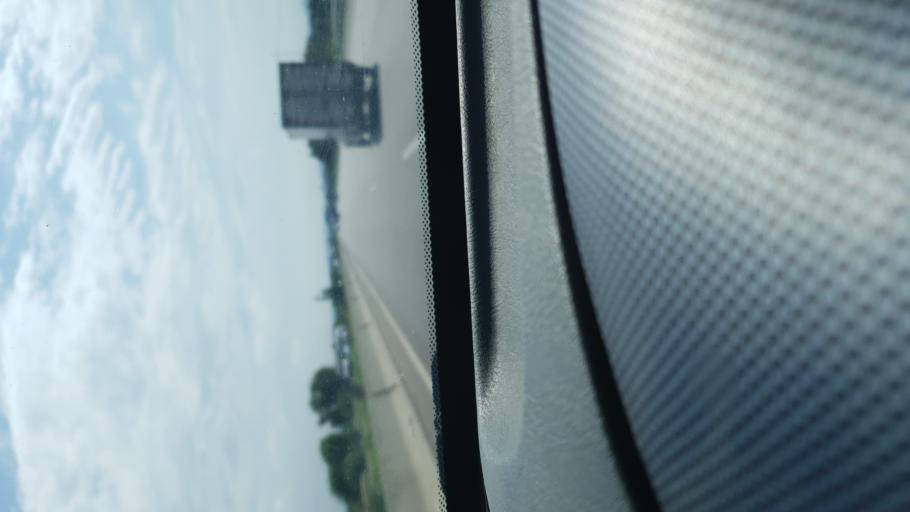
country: TN
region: Nabul
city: Bu `Urqub
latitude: 36.5739
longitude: 10.5041
